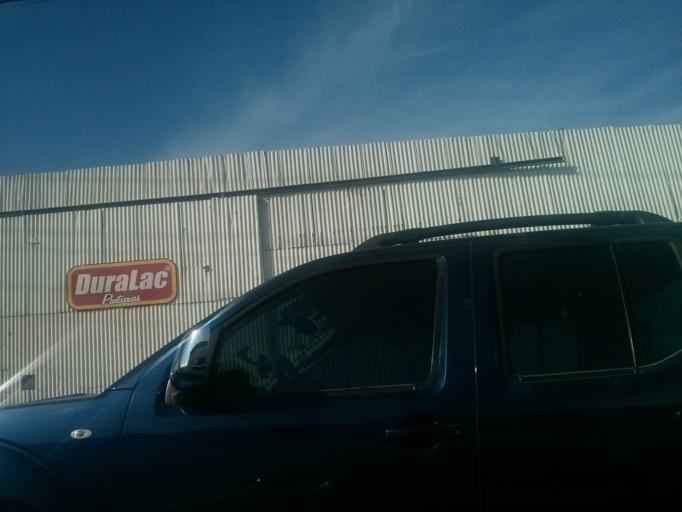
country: CR
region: San Jose
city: Colima
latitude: 9.9476
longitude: -84.0892
